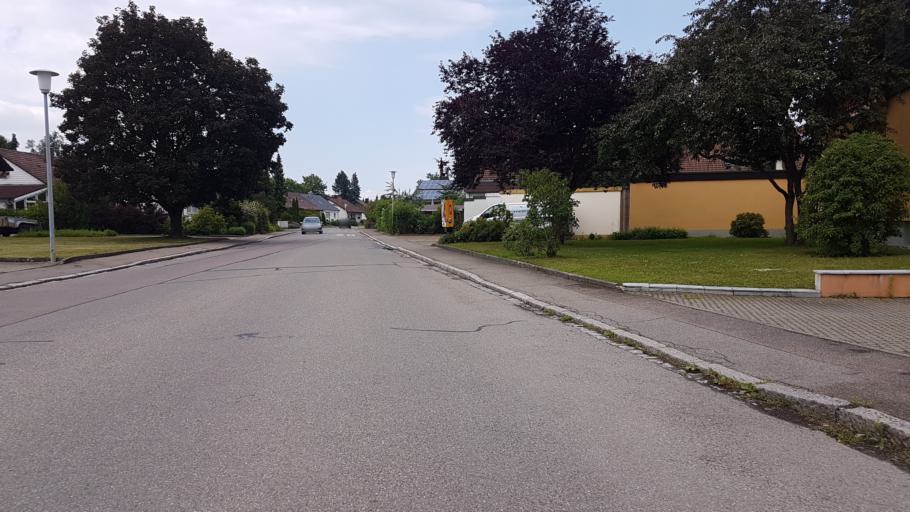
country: DE
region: Baden-Wuerttemberg
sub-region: Freiburg Region
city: Hufingen
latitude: 47.9215
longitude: 8.4982
